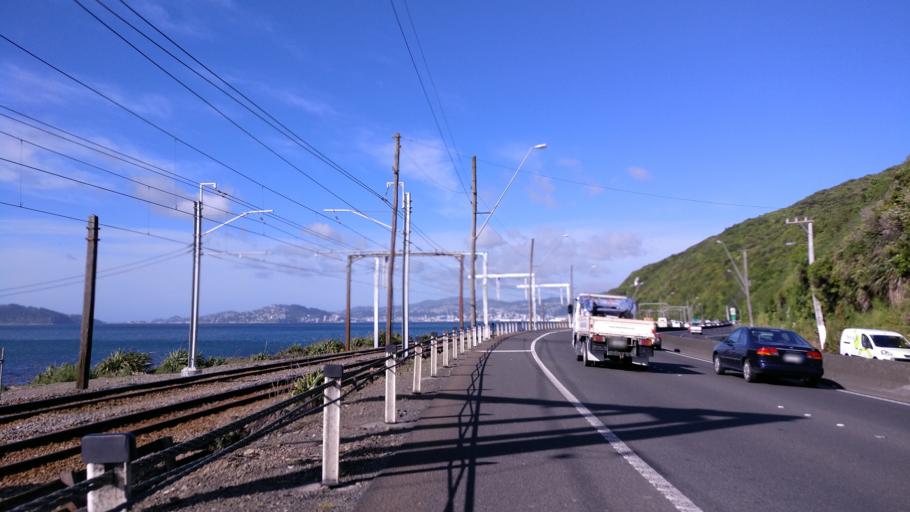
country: NZ
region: Wellington
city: Petone
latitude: -41.2309
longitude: 174.8412
